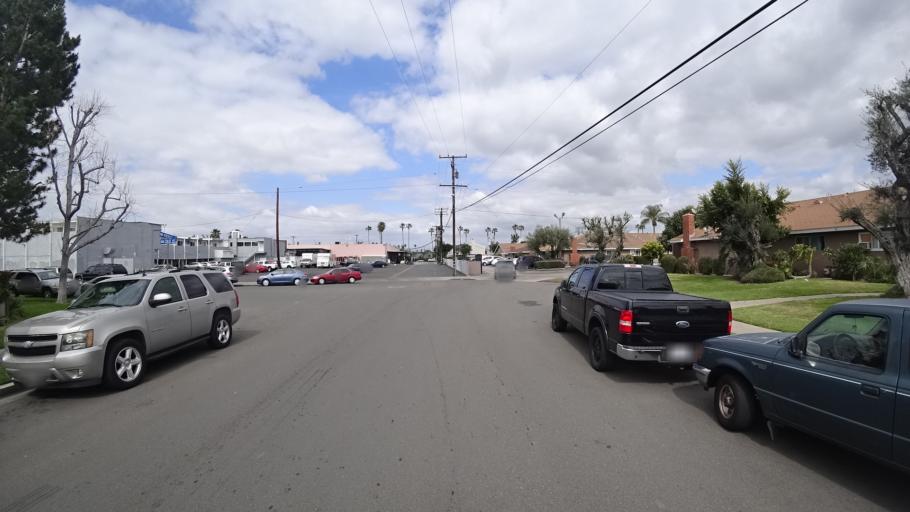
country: US
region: California
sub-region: Orange County
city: Stanton
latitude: 33.8085
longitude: -117.9739
